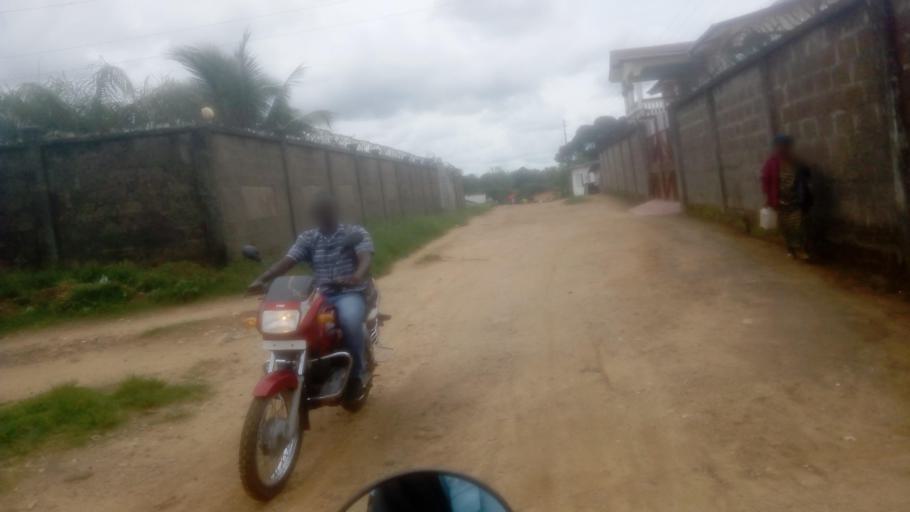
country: SL
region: Southern Province
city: Bo
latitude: 7.9403
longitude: -11.7303
